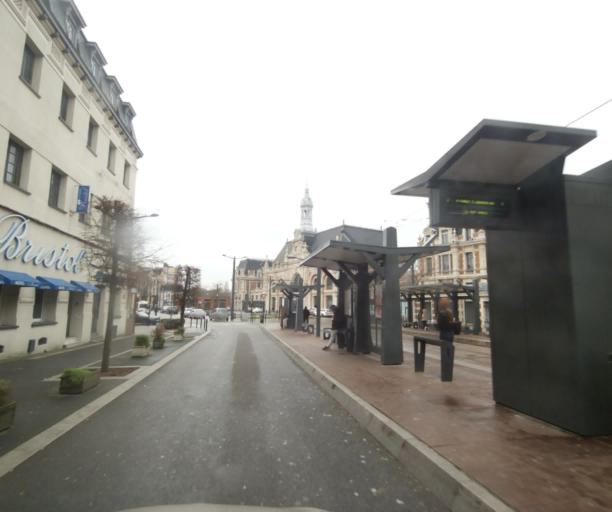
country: FR
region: Nord-Pas-de-Calais
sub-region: Departement du Nord
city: Anzin
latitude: 50.3639
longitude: 3.5182
